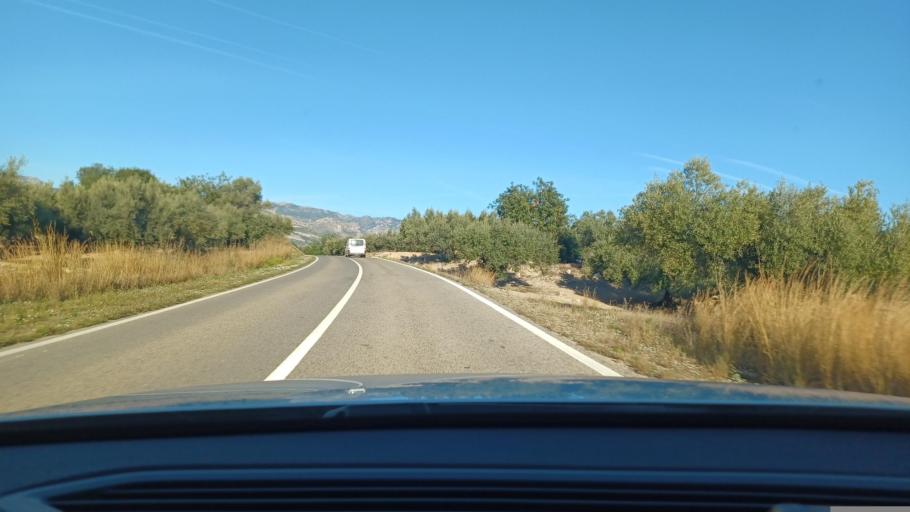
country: ES
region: Catalonia
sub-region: Provincia de Tarragona
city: Mas de Barberans
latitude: 40.7171
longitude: 0.4017
